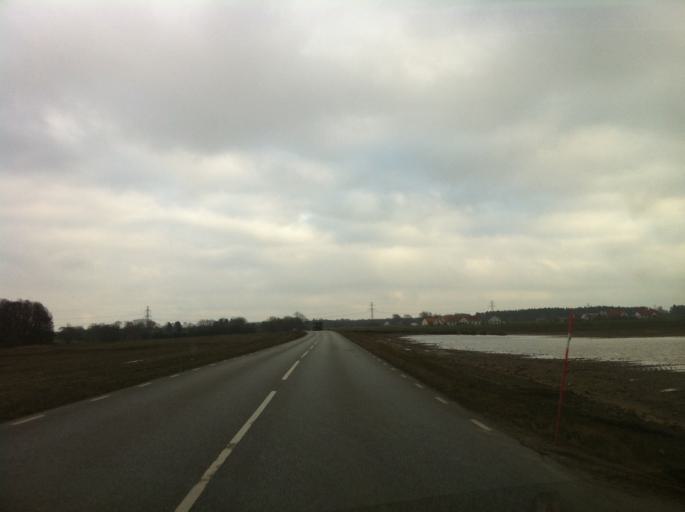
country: SE
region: Skane
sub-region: Kavlinge Kommun
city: Hofterup
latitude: 55.8250
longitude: 12.9846
